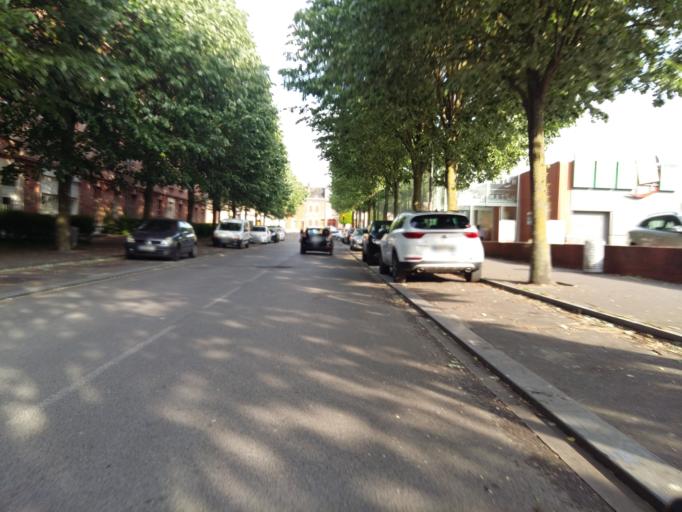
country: FR
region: Picardie
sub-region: Departement de la Somme
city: Amiens
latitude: 49.8894
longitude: 2.2795
